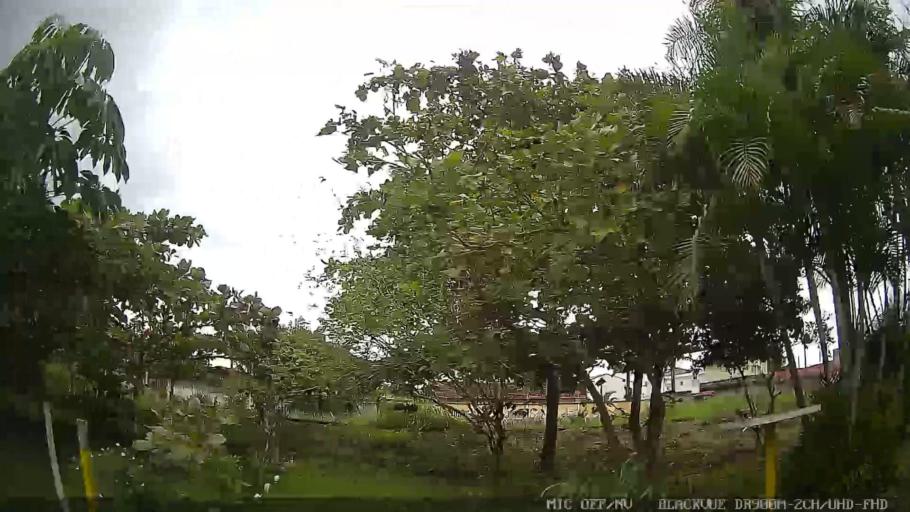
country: BR
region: Sao Paulo
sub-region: Itanhaem
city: Itanhaem
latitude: -24.1573
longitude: -46.7417
